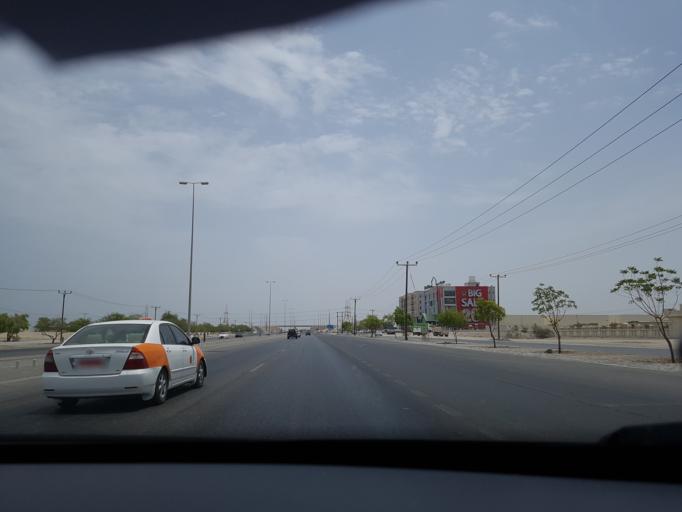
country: OM
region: Al Batinah
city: Barka'
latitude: 23.6762
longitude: 57.9963
